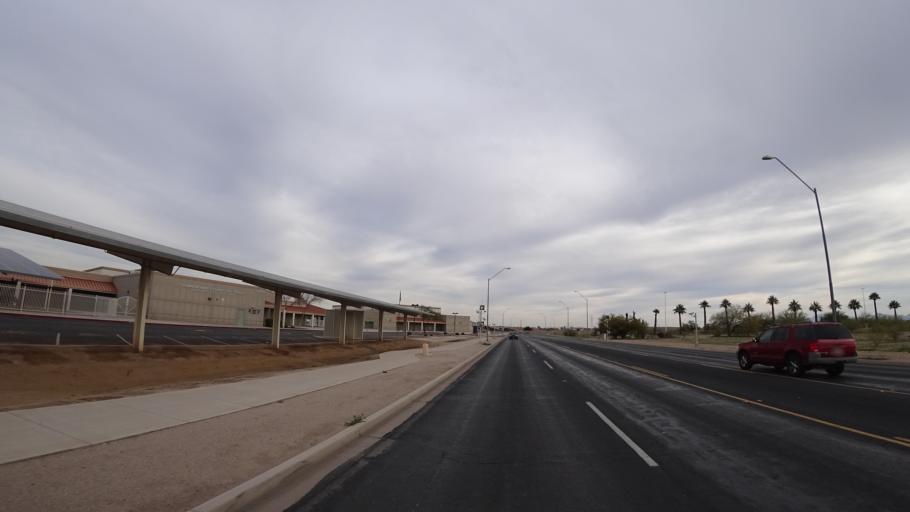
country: US
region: Arizona
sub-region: Maricopa County
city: El Mirage
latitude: 33.6170
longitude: -112.3146
